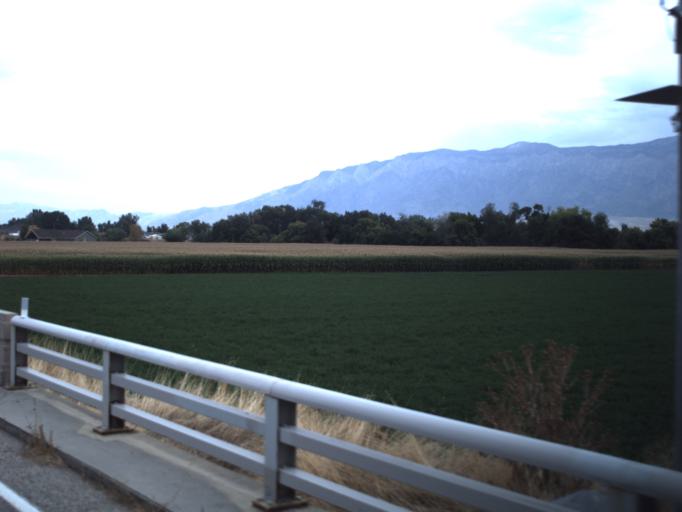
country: US
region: Utah
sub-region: Weber County
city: Plain City
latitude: 41.2784
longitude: -112.0925
